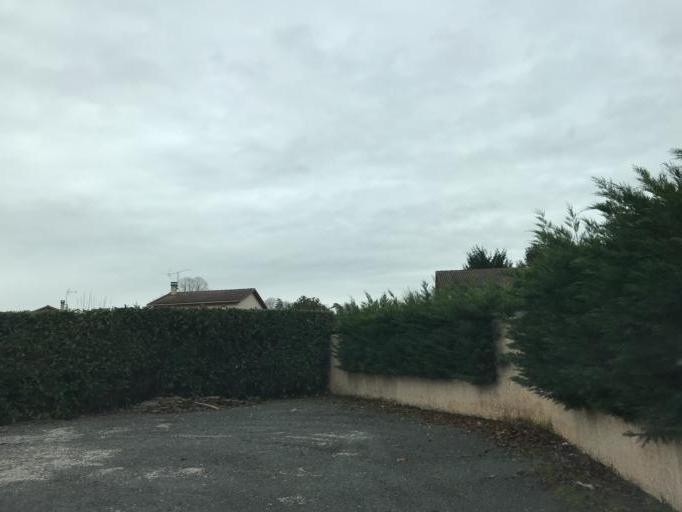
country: FR
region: Rhone-Alpes
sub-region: Departement de l'Ain
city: Sainte-Euphemie
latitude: 45.9718
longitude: 4.7974
